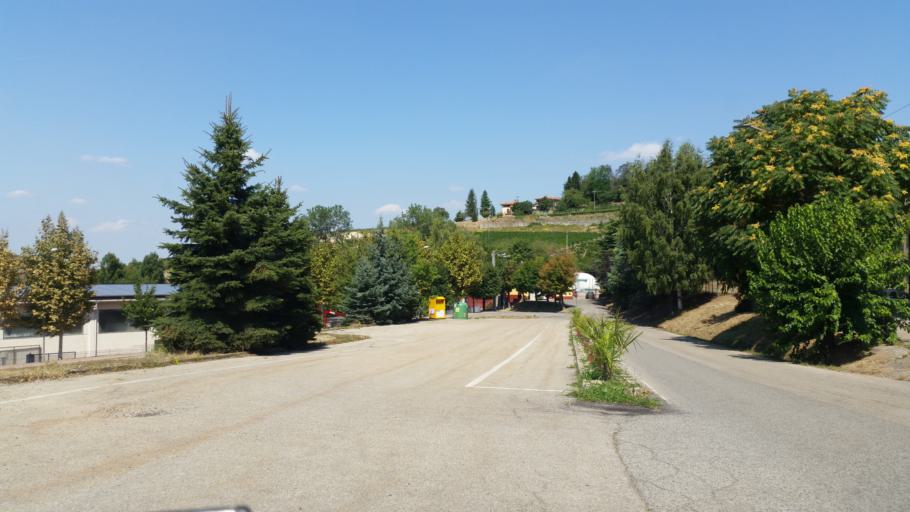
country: IT
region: Piedmont
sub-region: Provincia di Cuneo
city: Mango
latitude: 44.6864
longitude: 8.1552
